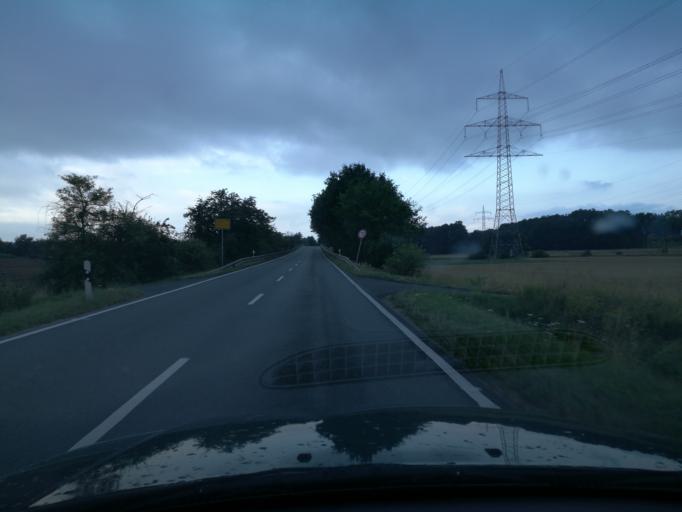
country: DE
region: Bavaria
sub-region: Regierungsbezirk Mittelfranken
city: Obermichelbach
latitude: 49.5597
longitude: 10.9587
